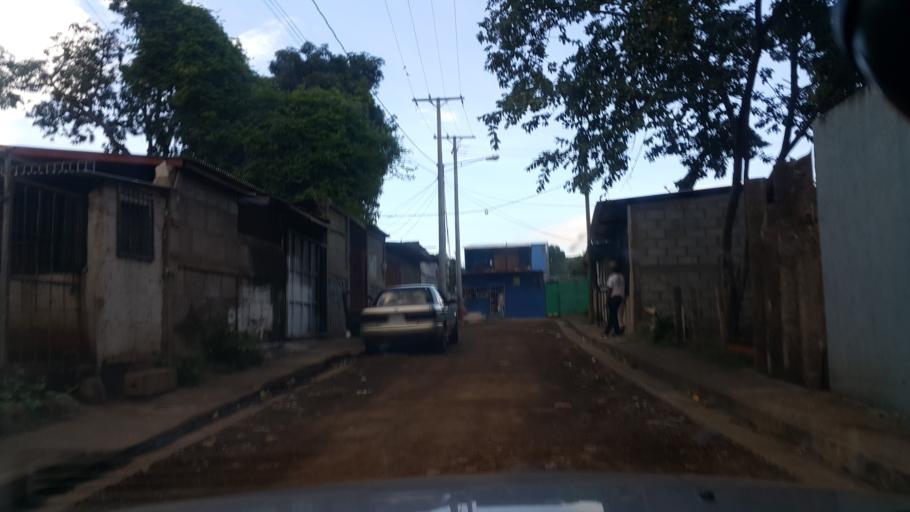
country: NI
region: Managua
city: Managua
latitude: 12.1158
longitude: -86.2404
